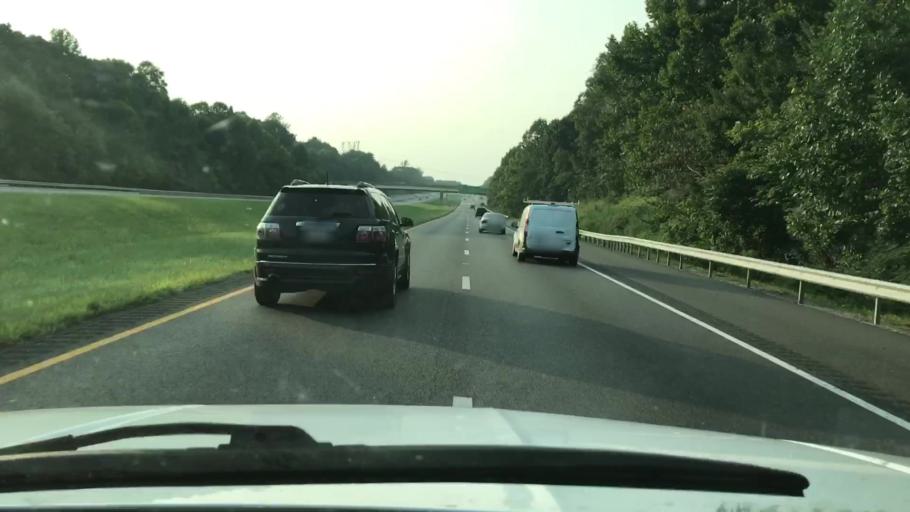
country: US
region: Virginia
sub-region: Chesterfield County
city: Brandermill
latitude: 37.4134
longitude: -77.6188
